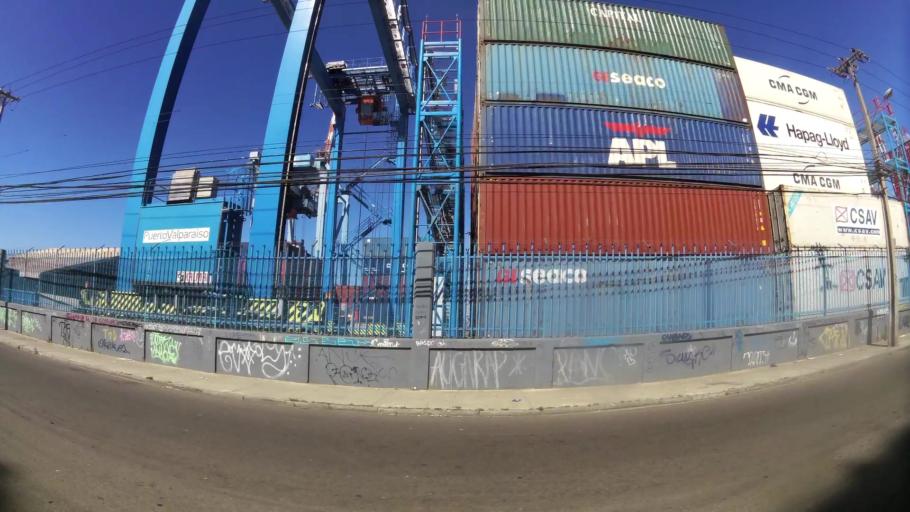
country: CL
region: Valparaiso
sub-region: Provincia de Valparaiso
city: Valparaiso
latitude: -33.0286
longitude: -71.6291
